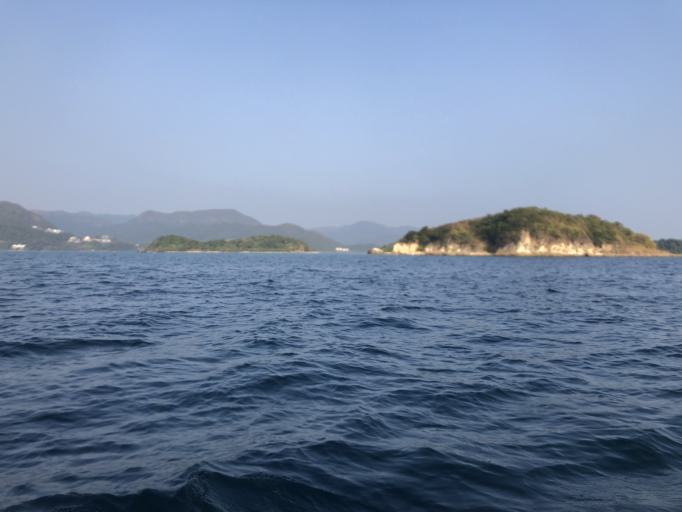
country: HK
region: Sai Kung
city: Sai Kung
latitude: 22.3738
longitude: 114.2819
